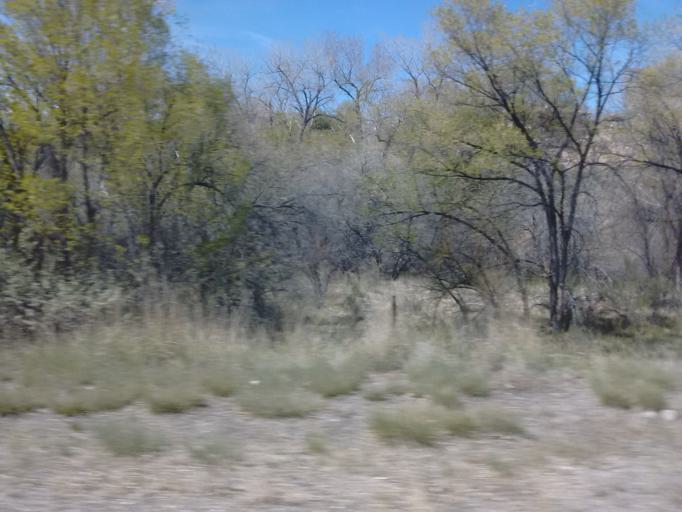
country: US
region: Colorado
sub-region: Mesa County
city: Redlands
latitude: 39.0792
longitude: -108.6336
